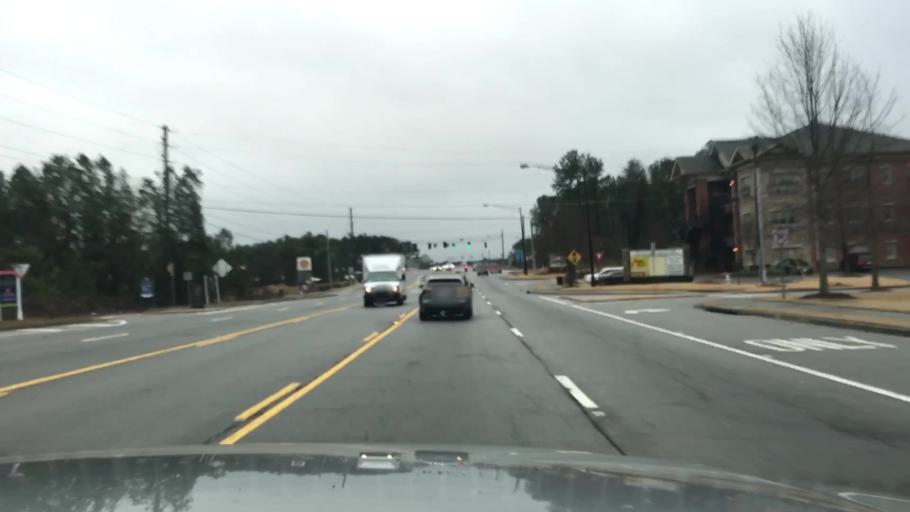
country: US
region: Georgia
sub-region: Gwinnett County
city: Dacula
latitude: 34.0779
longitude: -83.9179
